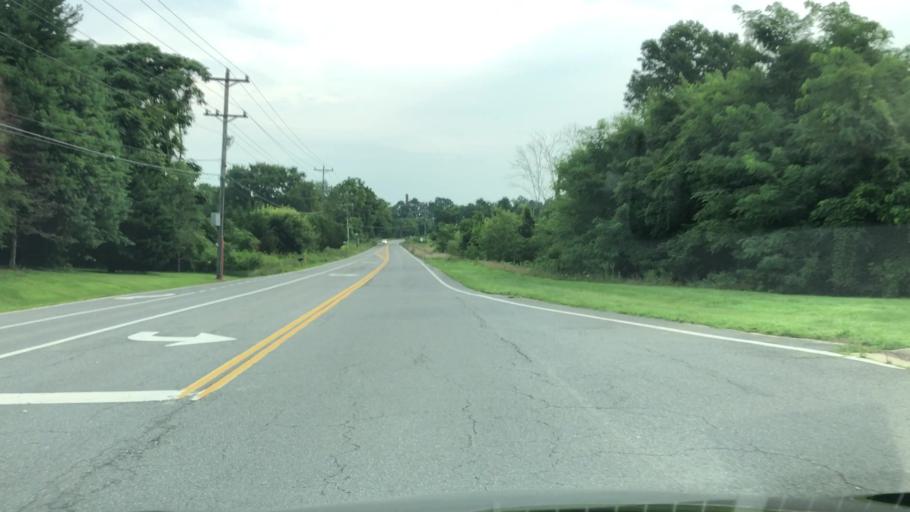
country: US
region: Virginia
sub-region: Fauquier County
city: New Baltimore
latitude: 38.7357
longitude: -77.6838
